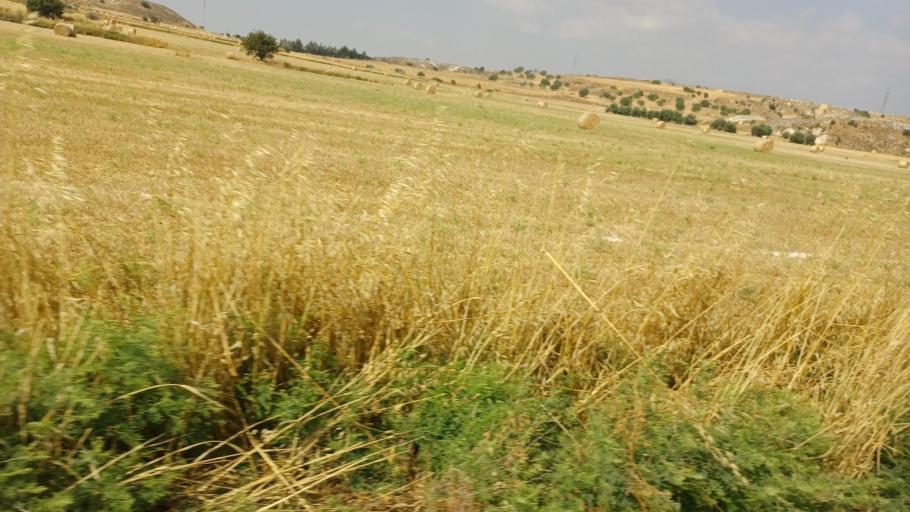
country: CY
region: Larnaka
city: Aradippou
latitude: 34.9191
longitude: 33.5381
